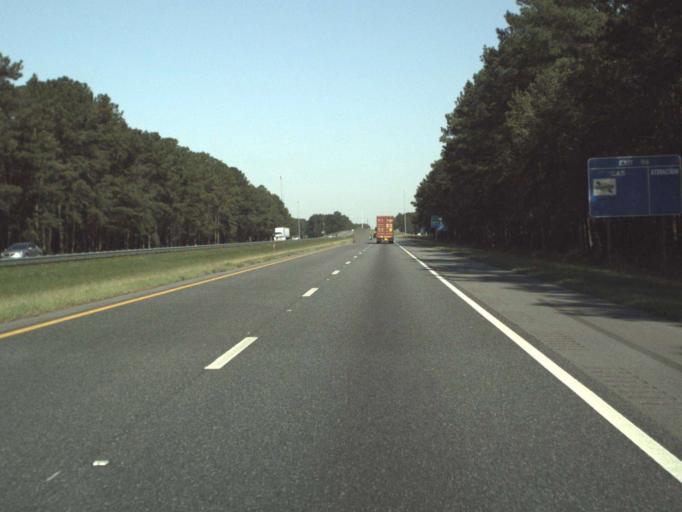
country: US
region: Florida
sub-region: Walton County
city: DeFuniak Springs
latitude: 30.7098
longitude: -85.9441
